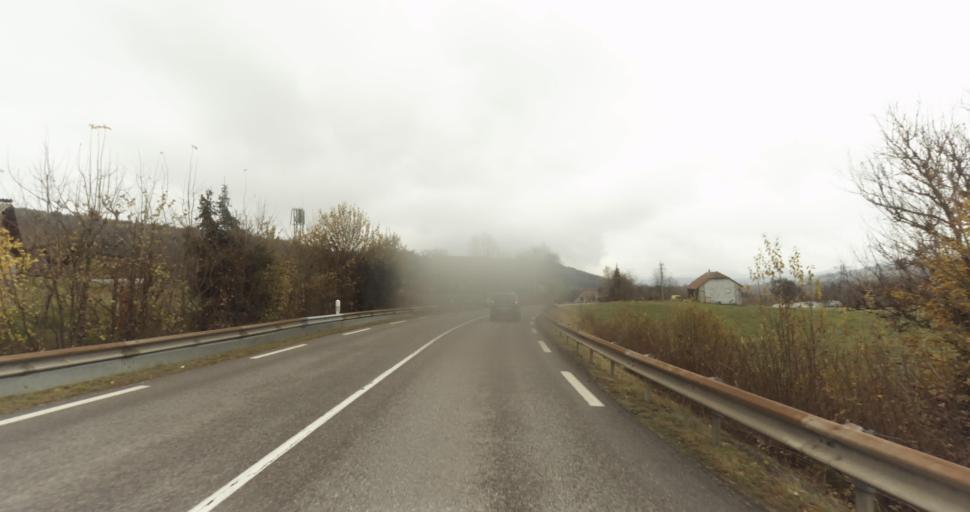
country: FR
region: Rhone-Alpes
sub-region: Departement de la Haute-Savoie
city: Evires
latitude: 46.0252
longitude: 6.2369
